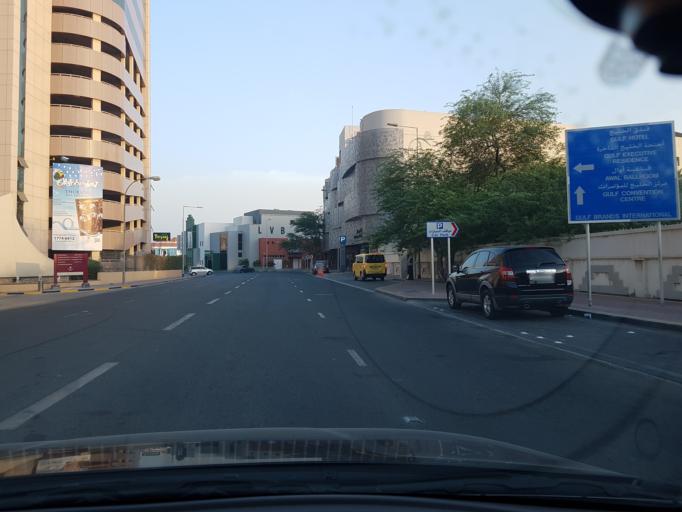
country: BH
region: Manama
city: Manama
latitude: 26.2156
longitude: 50.5938
